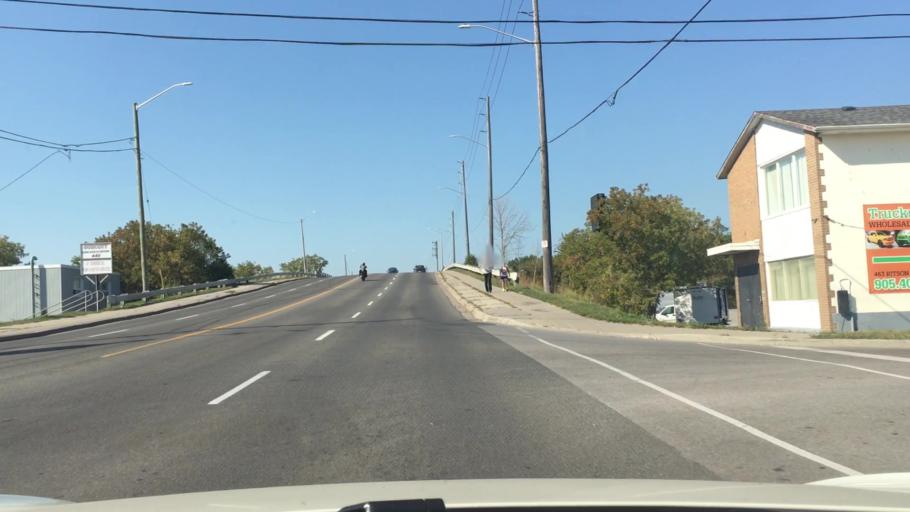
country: CA
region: Ontario
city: Oshawa
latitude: 43.8878
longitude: -78.8483
